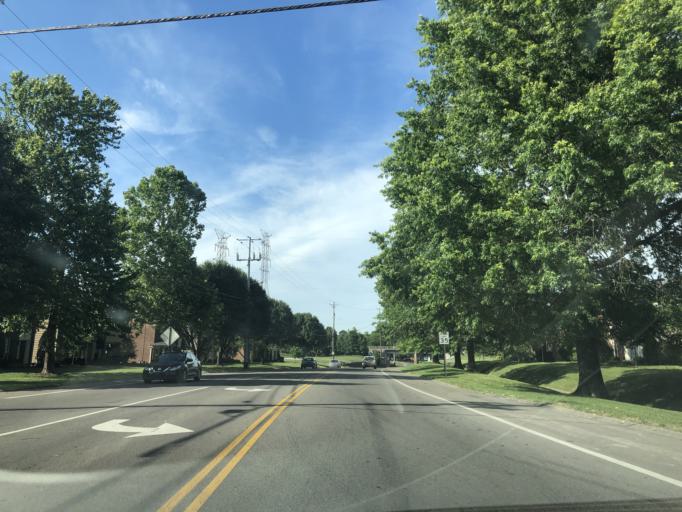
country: US
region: Tennessee
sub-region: Davidson County
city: Belle Meade
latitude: 36.0682
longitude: -86.9493
